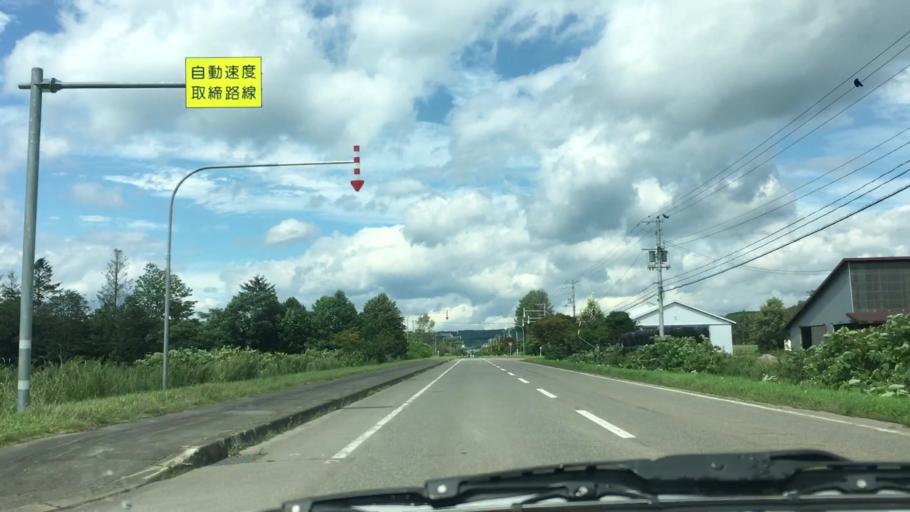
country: JP
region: Hokkaido
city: Otofuke
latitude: 43.2892
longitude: 143.3078
